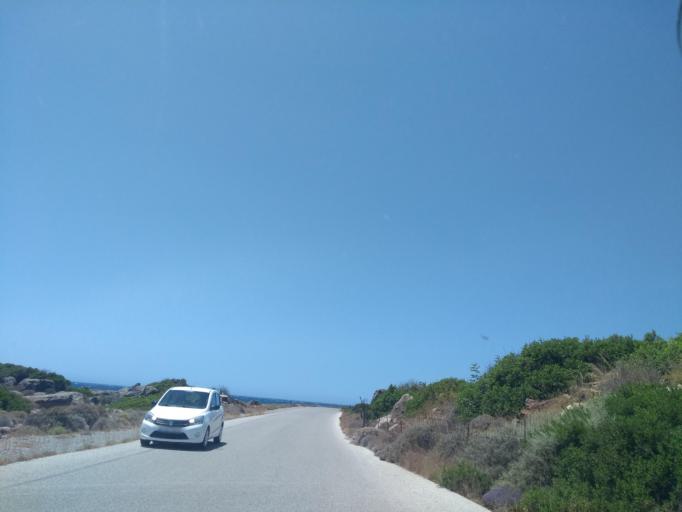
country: GR
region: Crete
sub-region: Nomos Chanias
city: Vryses
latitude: 35.3502
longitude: 23.5380
